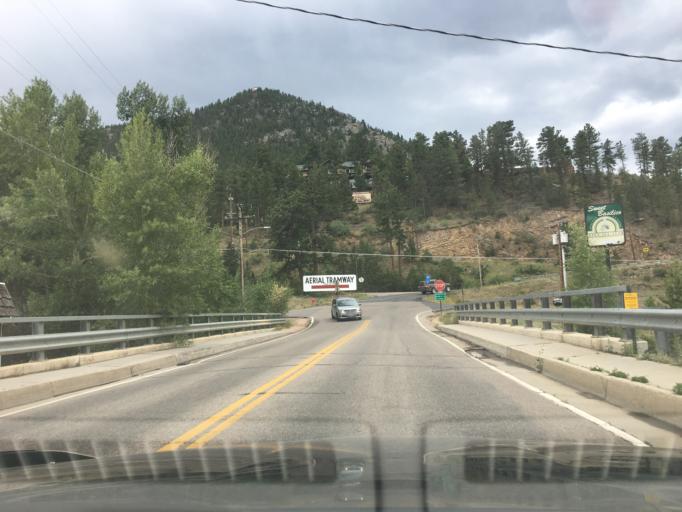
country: US
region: Colorado
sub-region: Larimer County
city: Estes Park
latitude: 40.3718
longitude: -105.5236
